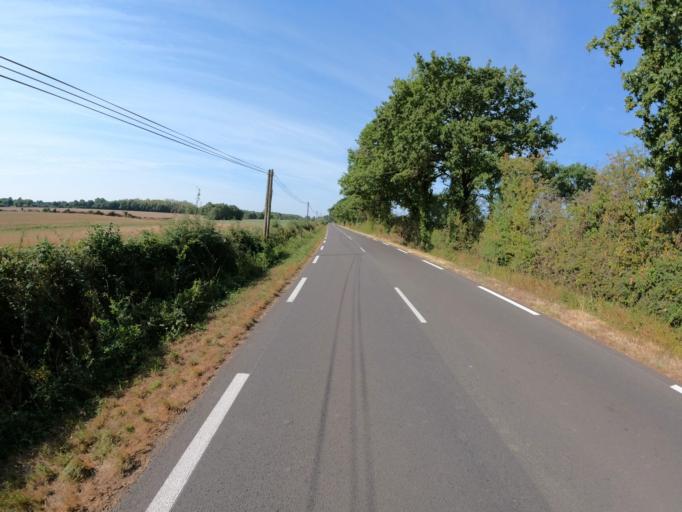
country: FR
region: Pays de la Loire
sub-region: Departement de la Vendee
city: Saint-Christophe-du-Ligneron
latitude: 46.8360
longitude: -1.7537
